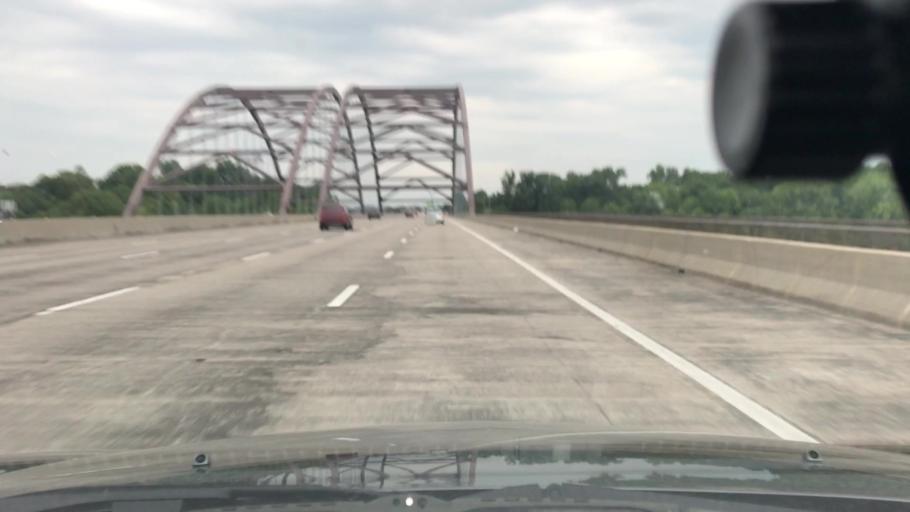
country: US
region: Missouri
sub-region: Saint Charles County
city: Saint Charles
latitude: 38.7355
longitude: -90.5210
